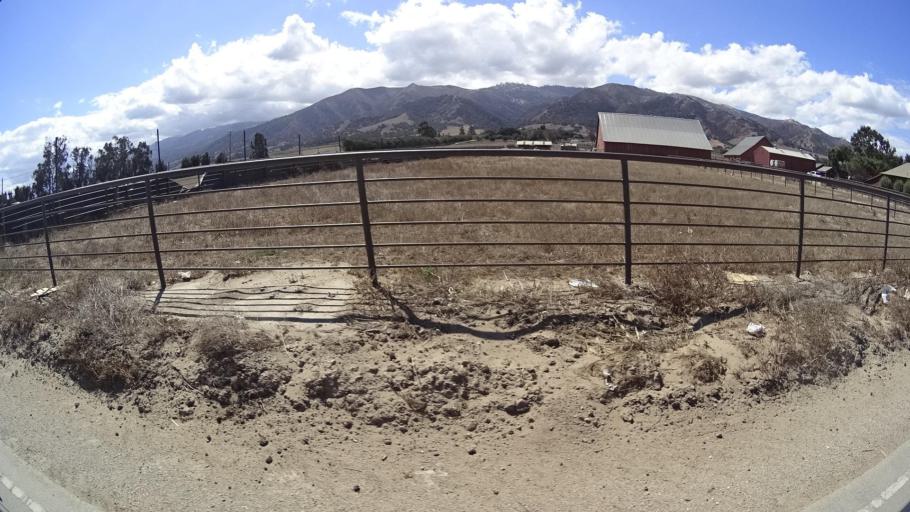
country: US
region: California
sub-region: Monterey County
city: Chualar
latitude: 36.5617
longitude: -121.5539
